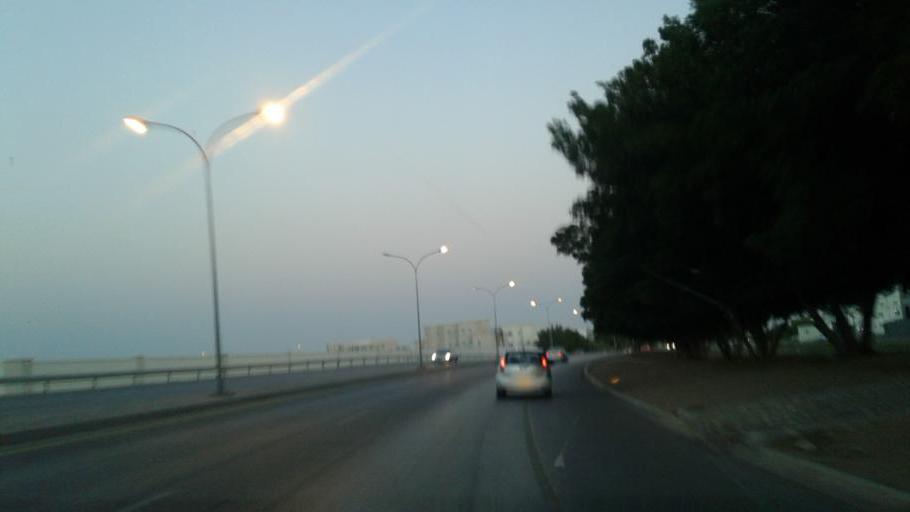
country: OM
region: Muhafazat Masqat
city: As Sib al Jadidah
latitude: 23.6129
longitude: 58.2358
